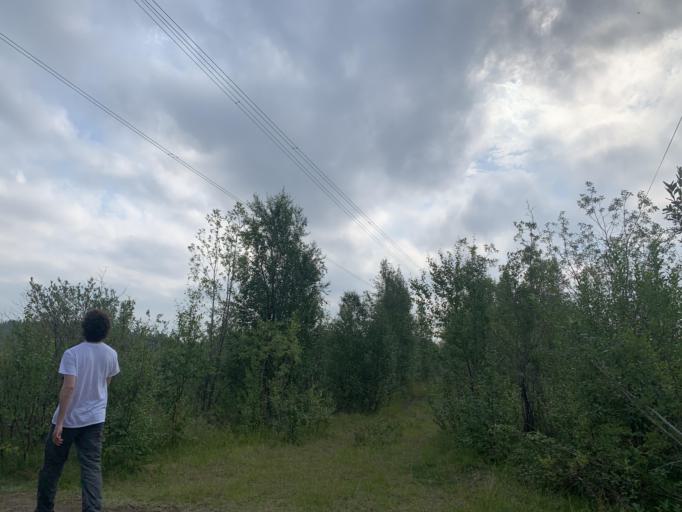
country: RU
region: Murmansk
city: Monchegorsk
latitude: 67.7967
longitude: 32.7916
